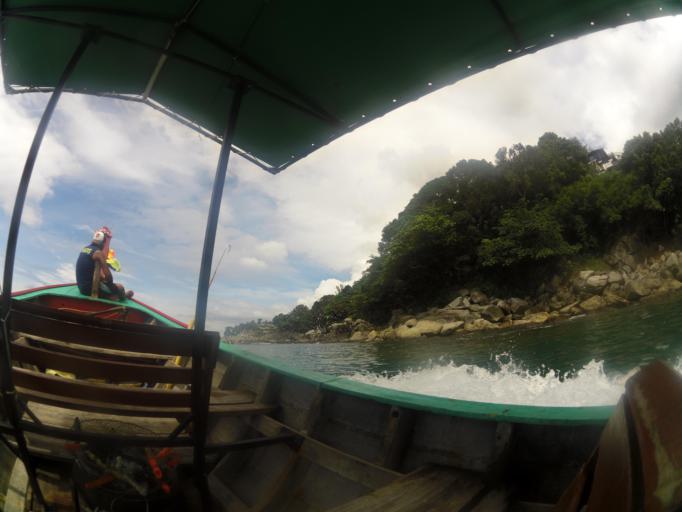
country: TH
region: Phuket
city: Patong
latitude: 7.9631
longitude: 98.2801
